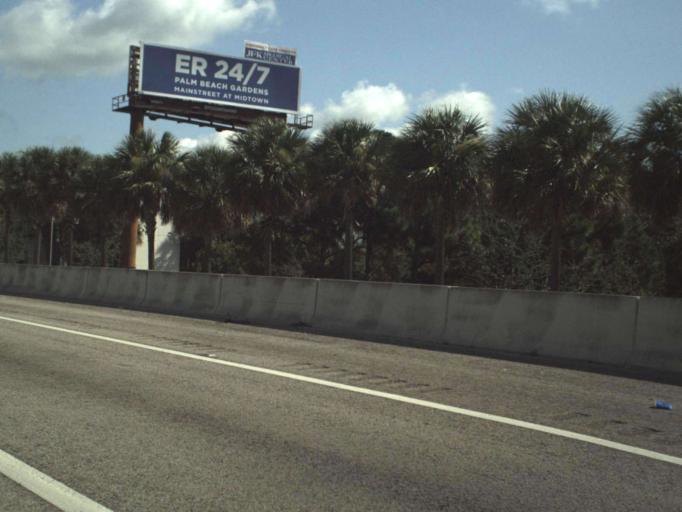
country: US
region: Florida
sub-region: Palm Beach County
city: North Palm Beach
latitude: 26.8347
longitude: -80.0985
